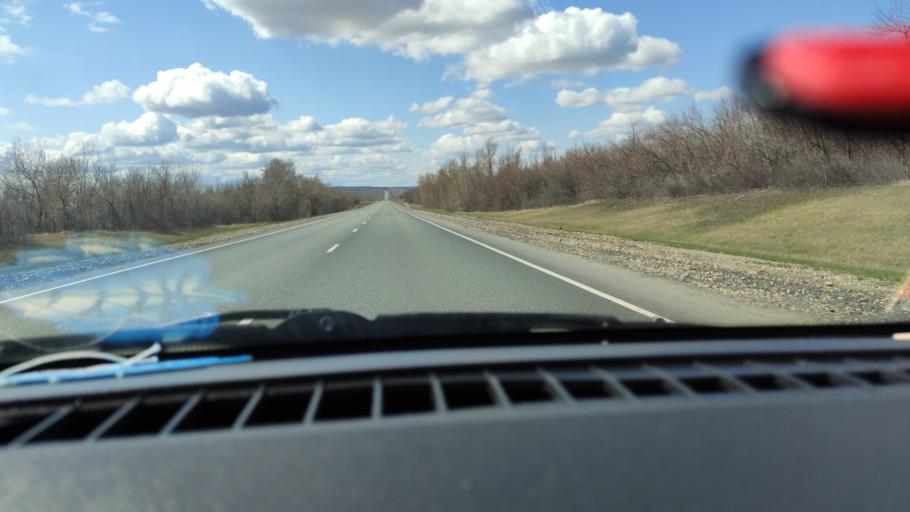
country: RU
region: Saratov
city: Khvalynsk
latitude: 52.5882
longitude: 48.1268
